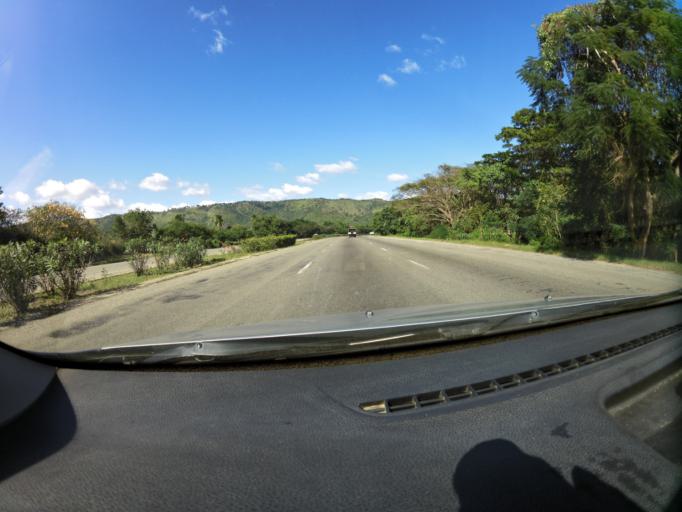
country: CU
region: Santiago de Cuba
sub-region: Municipio de Santiago de Cuba
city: Santiago de Cuba
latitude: 20.0768
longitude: -75.8006
